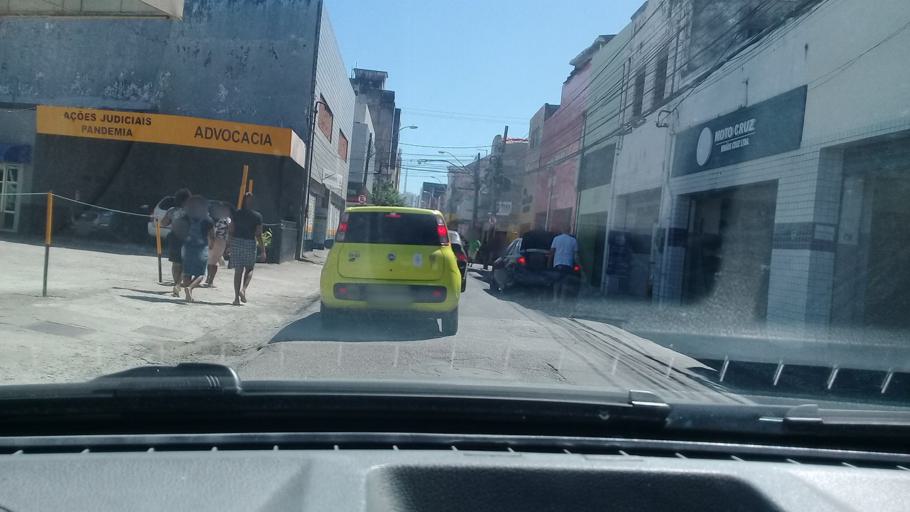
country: BR
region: Pernambuco
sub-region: Recife
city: Recife
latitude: -8.0685
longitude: -34.8823
